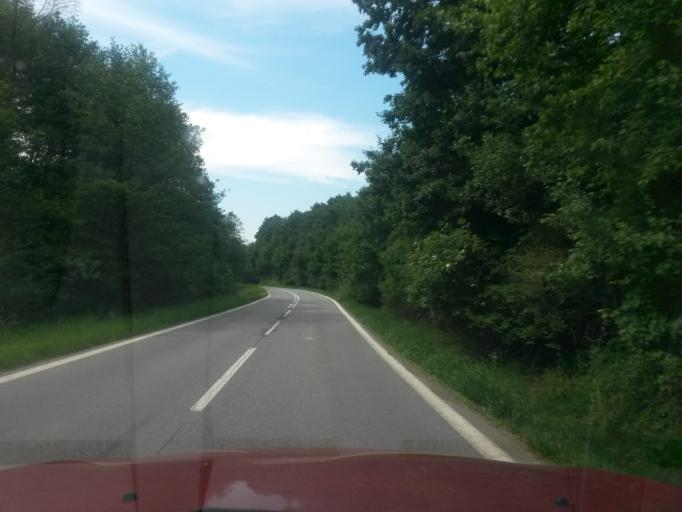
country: SK
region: Presovsky
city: Snina
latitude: 48.9919
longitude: 22.2395
